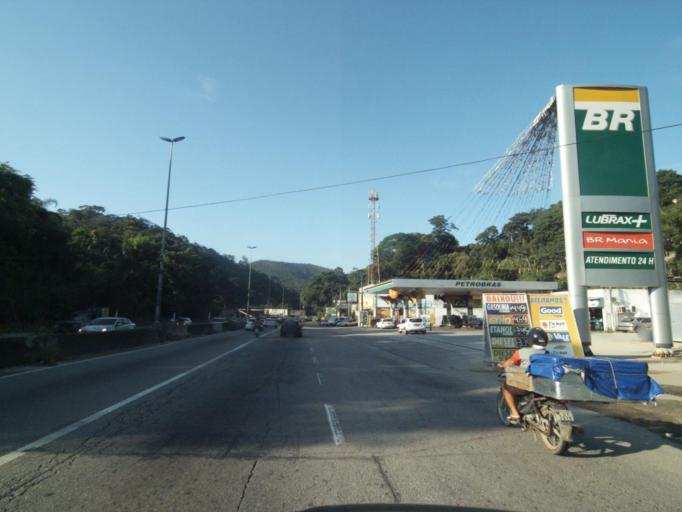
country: BR
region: Rio de Janeiro
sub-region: Niteroi
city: Niteroi
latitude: -22.8765
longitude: -43.0550
